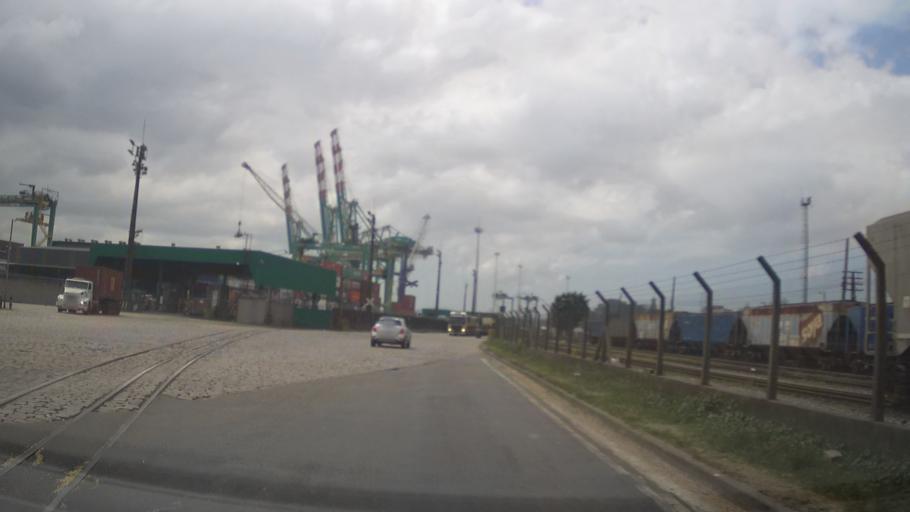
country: BR
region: Sao Paulo
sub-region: Santos
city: Santos
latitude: -23.9283
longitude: -46.3381
